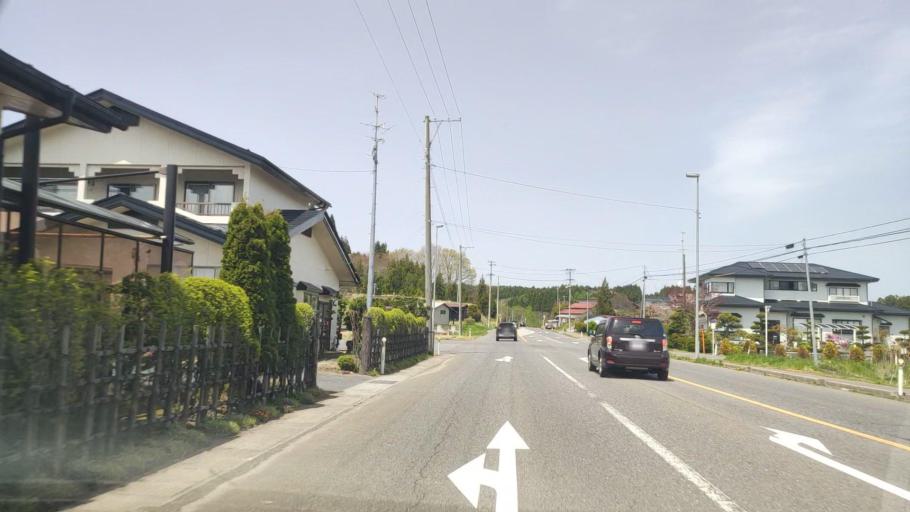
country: JP
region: Aomori
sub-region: Misawa Shi
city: Inuotose
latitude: 40.5603
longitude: 141.3847
